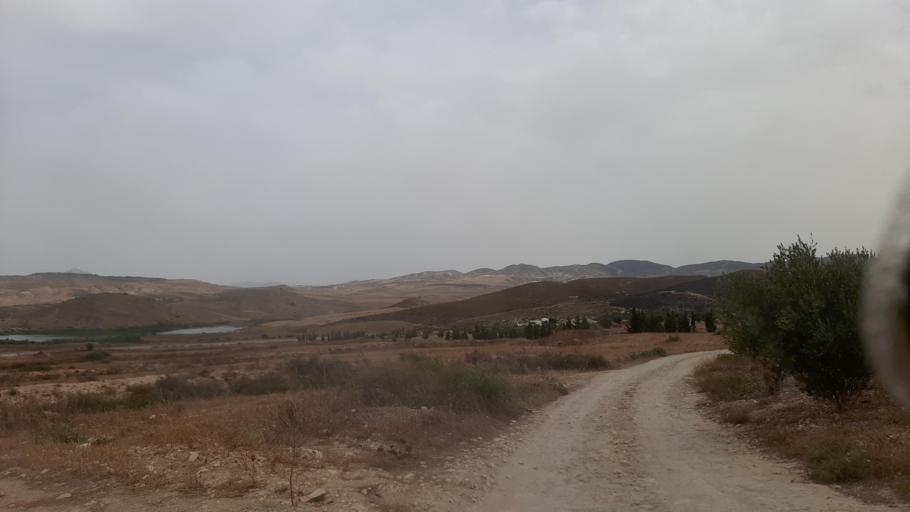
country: TN
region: Tunis
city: La Mohammedia
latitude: 36.5666
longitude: 10.1463
